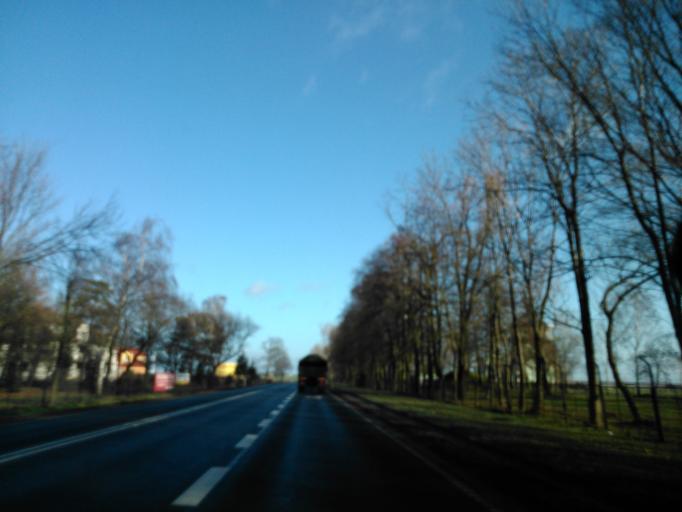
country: PL
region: Kujawsko-Pomorskie
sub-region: Powiat inowroclawski
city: Inowroclaw
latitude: 52.8272
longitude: 18.3071
